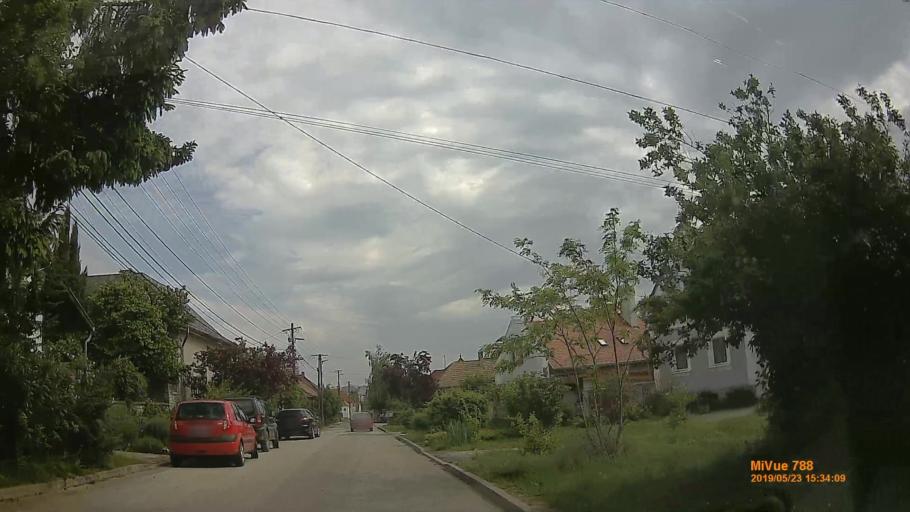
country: HU
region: Veszprem
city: Veszprem
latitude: 47.1015
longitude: 17.9032
